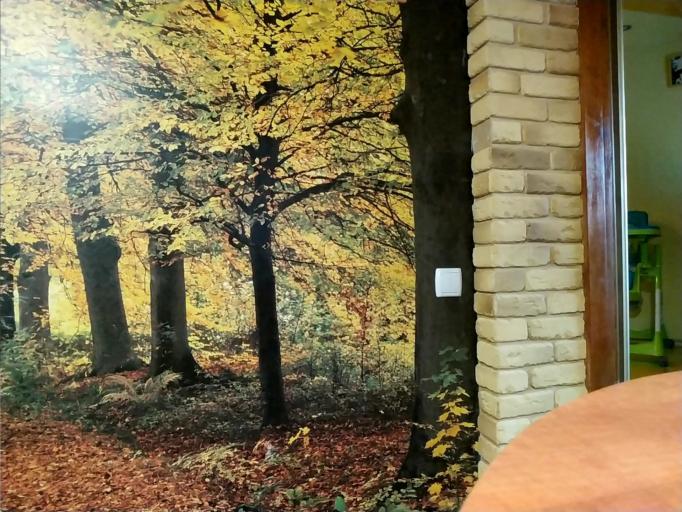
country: BY
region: Minsk
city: Il'ya
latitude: 54.4217
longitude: 27.4538
